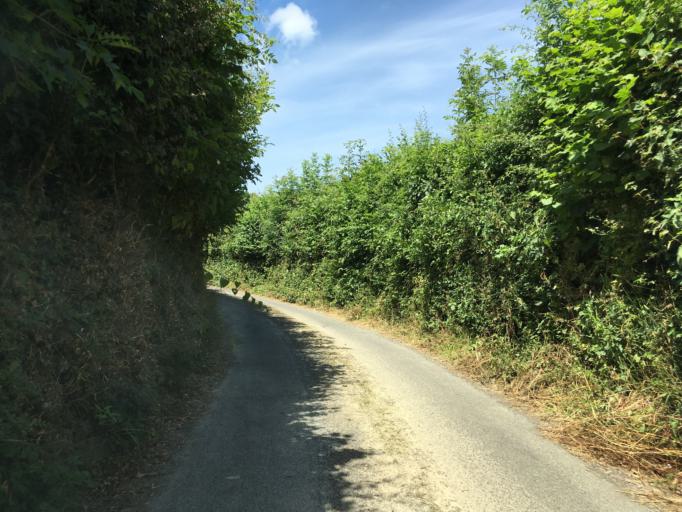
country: GB
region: Wales
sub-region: Newport
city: Llanwern
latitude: 51.5929
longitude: -2.9120
